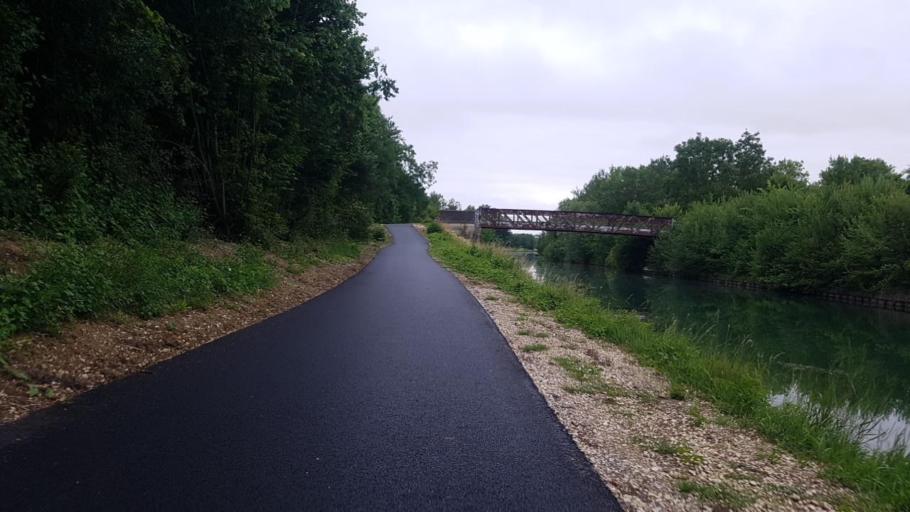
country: FR
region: Champagne-Ardenne
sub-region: Departement de la Marne
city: Vitry-le-Francois
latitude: 48.8258
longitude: 4.5152
